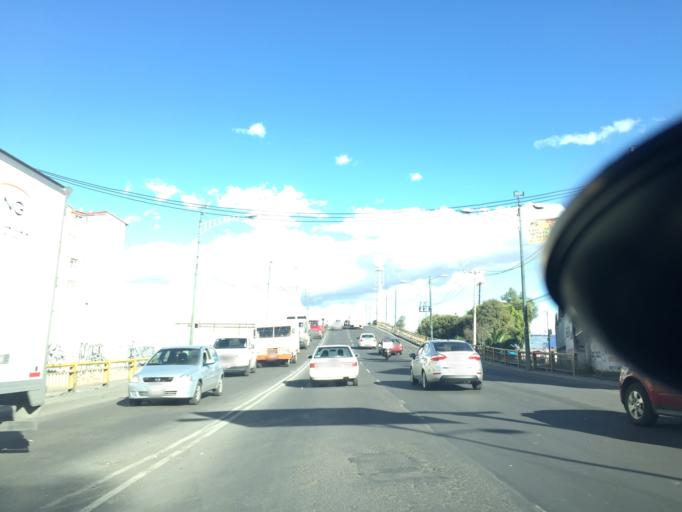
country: MX
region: Mexico City
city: Azcapotzalco
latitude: 19.4910
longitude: -99.1725
